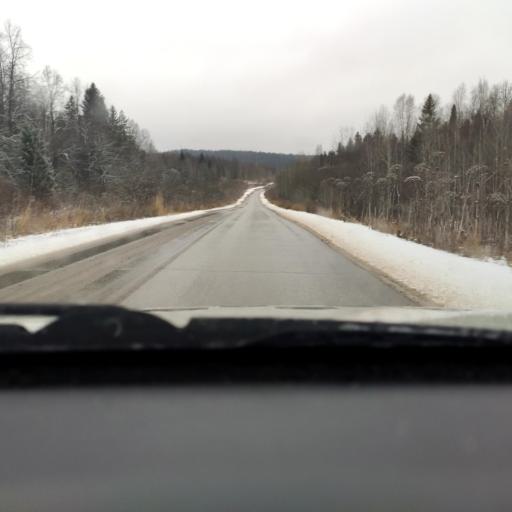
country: RU
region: Perm
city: Ferma
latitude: 57.9807
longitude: 56.3592
